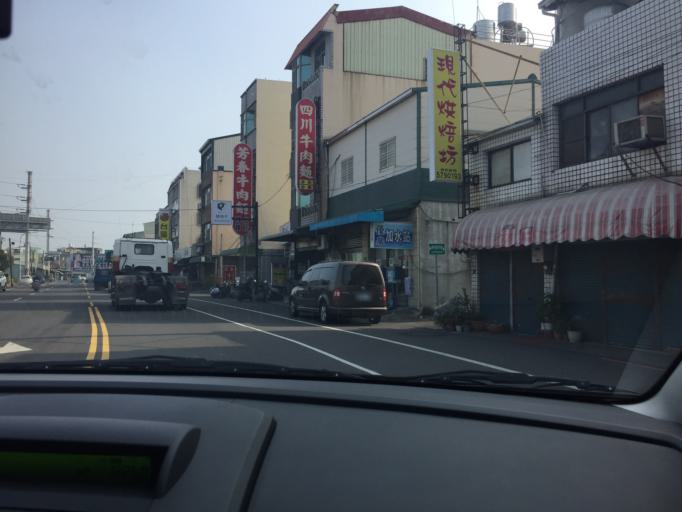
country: TW
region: Taiwan
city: Xinying
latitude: 23.1984
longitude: 120.3170
